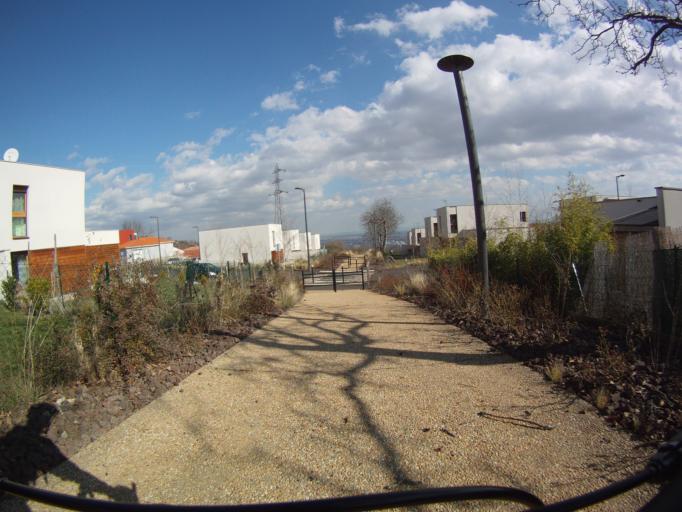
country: FR
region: Auvergne
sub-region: Departement du Puy-de-Dome
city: Ceyrat
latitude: 45.7482
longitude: 3.0603
